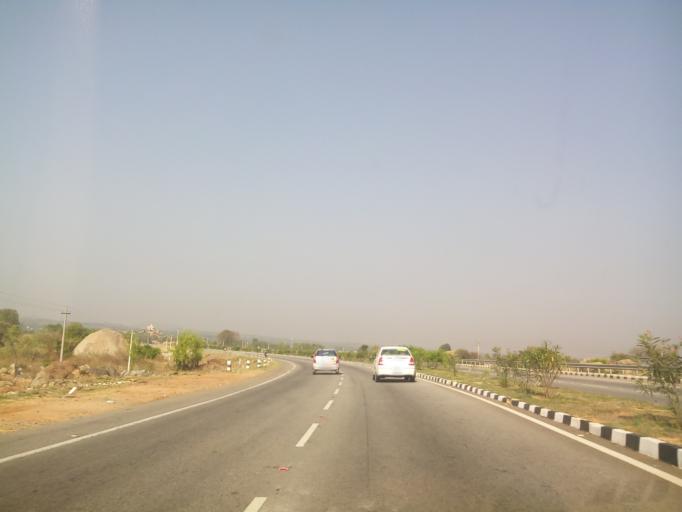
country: IN
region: Karnataka
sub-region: Bangalore Rural
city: Nelamangala
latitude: 13.0660
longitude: 77.2860
